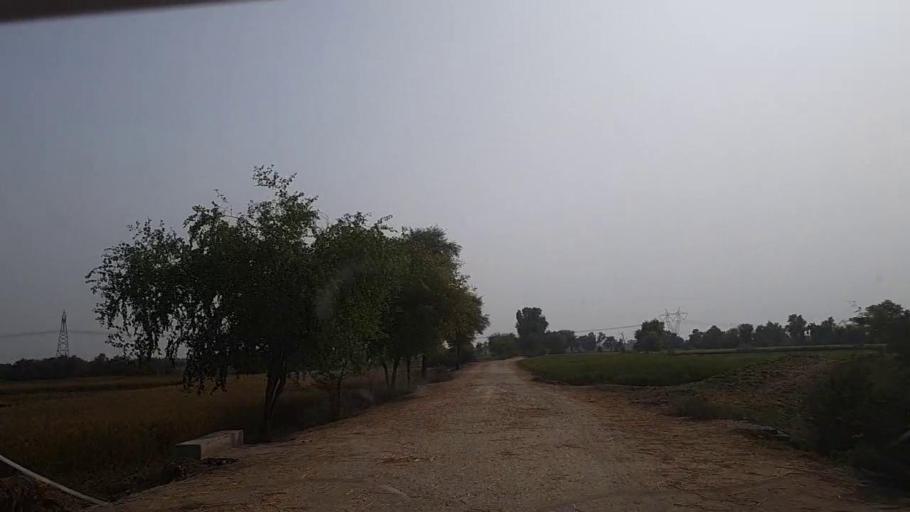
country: PK
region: Sindh
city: Madeji
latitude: 27.7422
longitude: 68.4359
